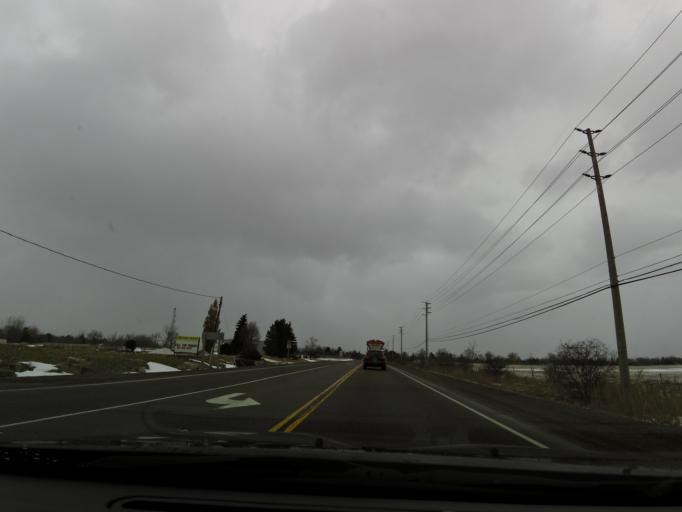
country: CA
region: Ontario
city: Ancaster
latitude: 43.3035
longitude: -79.9350
